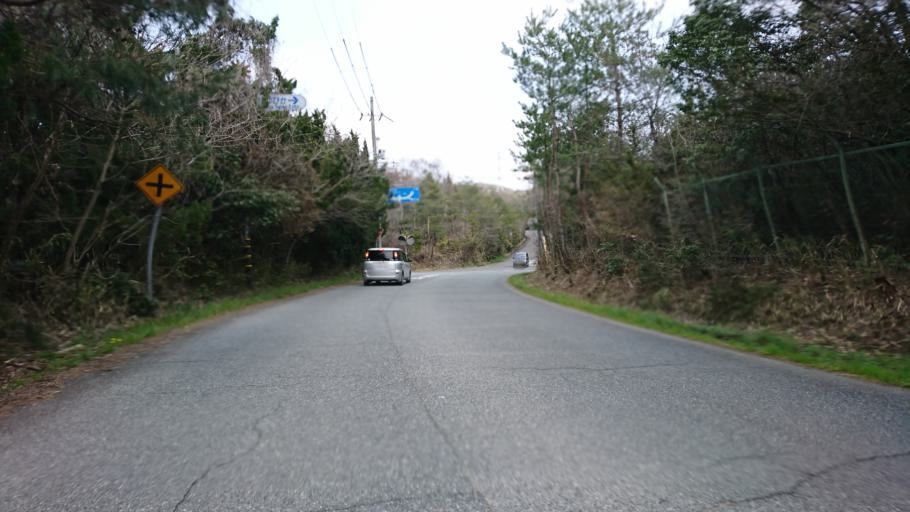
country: JP
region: Hyogo
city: Ono
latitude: 34.8176
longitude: 134.9027
